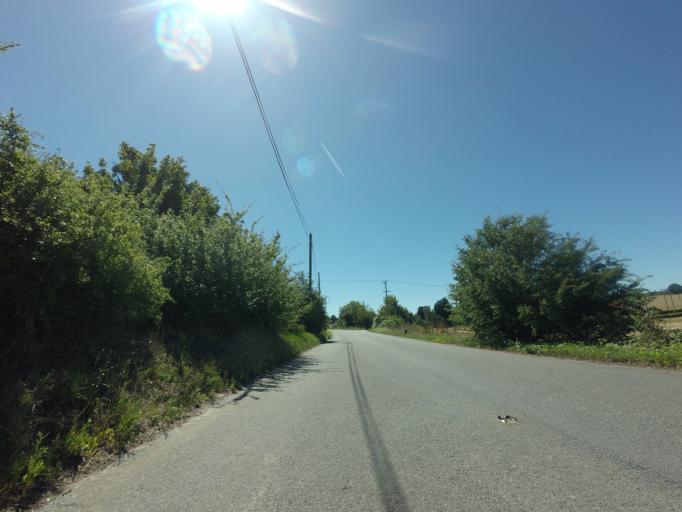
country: GB
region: England
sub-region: Kent
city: Eastry
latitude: 51.2143
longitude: 1.2997
